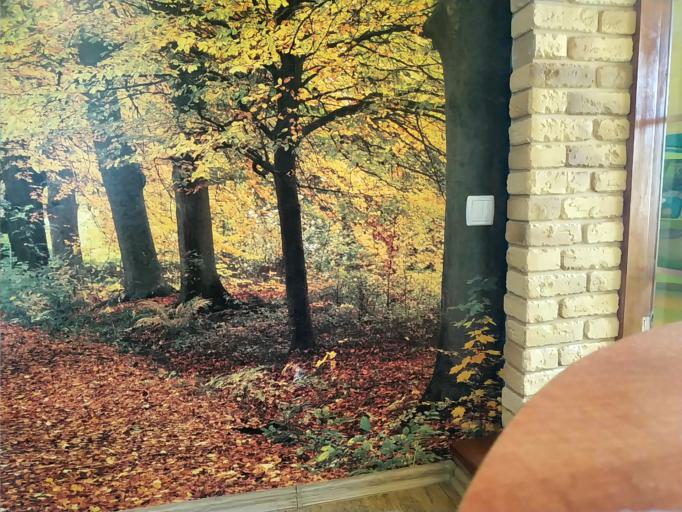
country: RU
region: Arkhangelskaya
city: Onega
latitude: 63.6977
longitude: 38.0900
